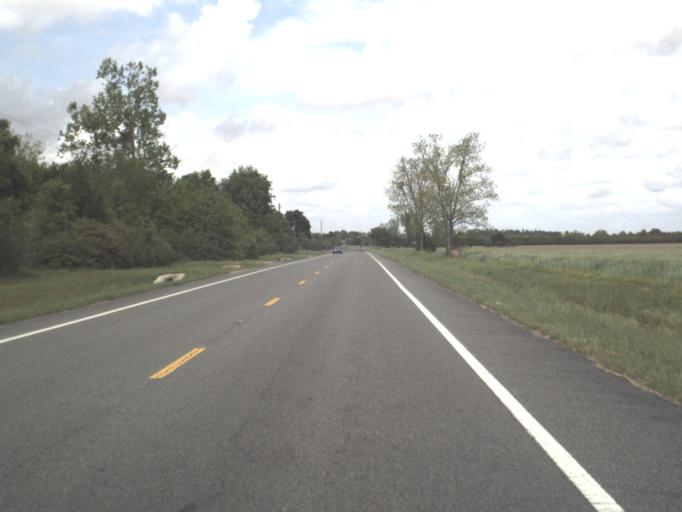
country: US
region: Florida
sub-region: Santa Rosa County
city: Point Baker
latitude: 30.7106
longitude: -87.0784
